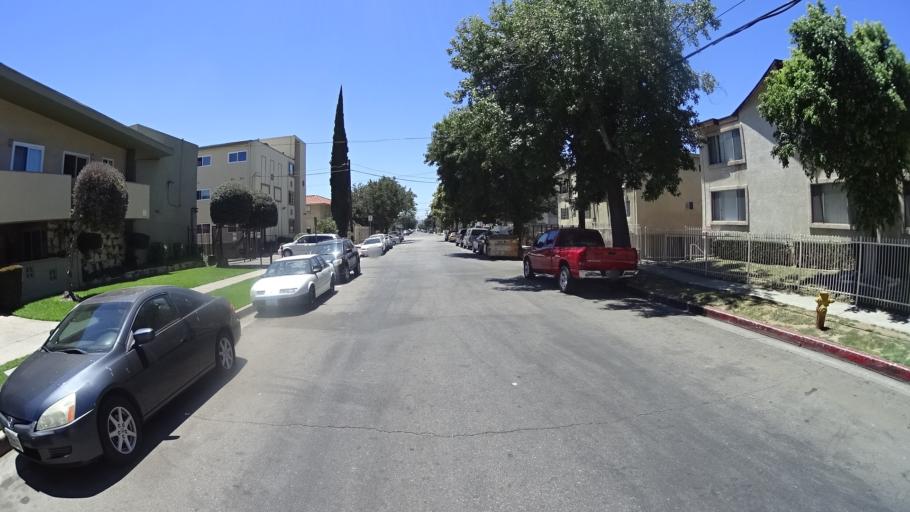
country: US
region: California
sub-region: Los Angeles County
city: Van Nuys
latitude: 34.2292
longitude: -118.4721
